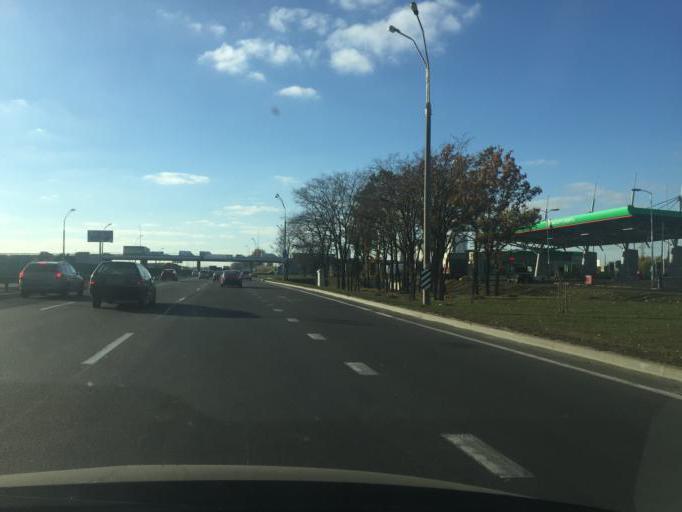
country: BY
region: Minsk
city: Machulishchy
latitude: 53.8335
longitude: 27.6048
